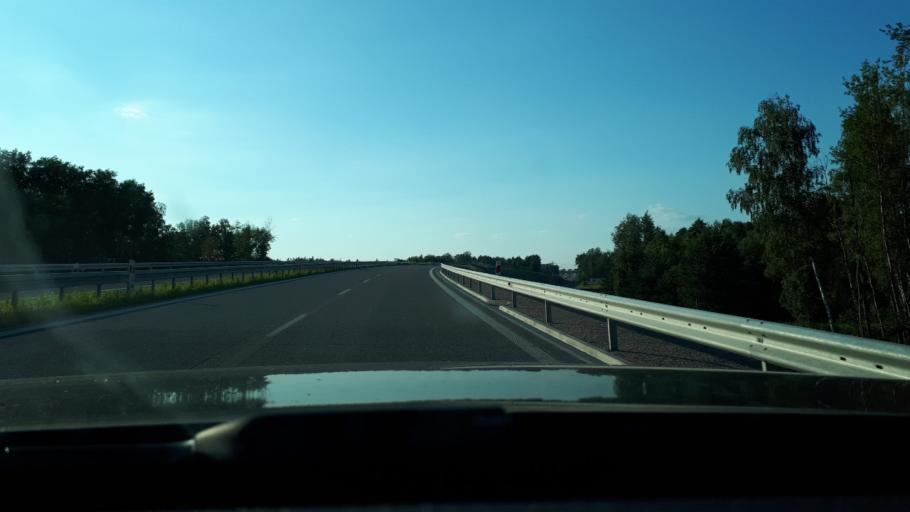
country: PL
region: Masovian Voivodeship
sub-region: Powiat piaseczynski
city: Gora Kalwaria
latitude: 51.9839
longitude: 21.1744
